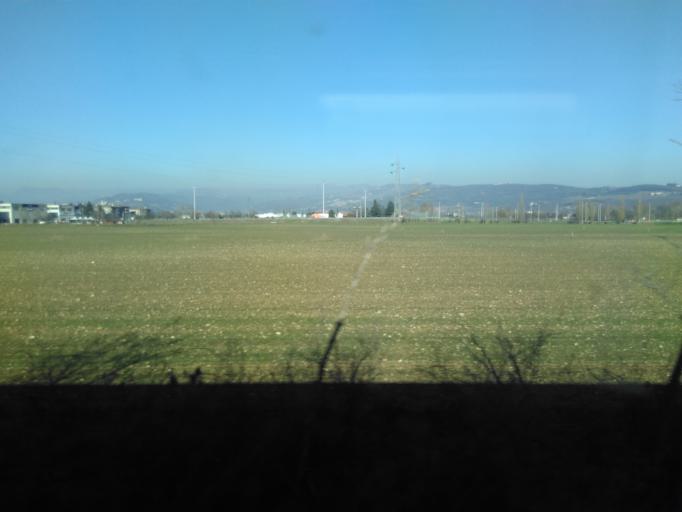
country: IT
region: Veneto
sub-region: Provincia di Verona
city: San Martino Buon Albergo
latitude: 45.4247
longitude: 11.0634
